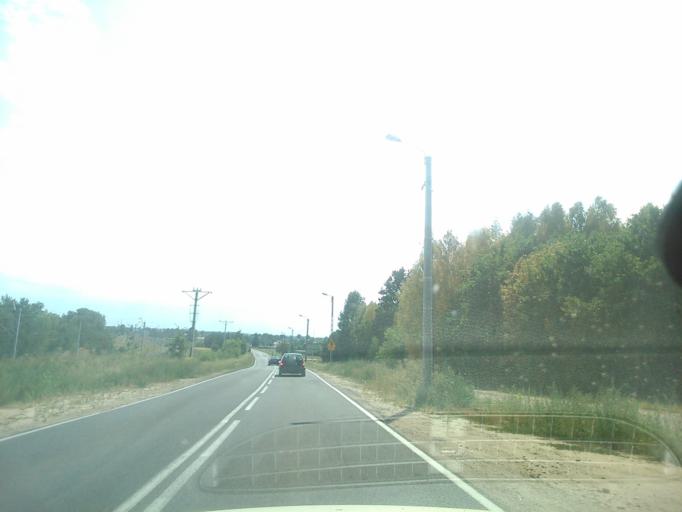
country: PL
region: Masovian Voivodeship
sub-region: Powiat mlawski
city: Mlawa
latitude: 53.1417
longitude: 20.3394
